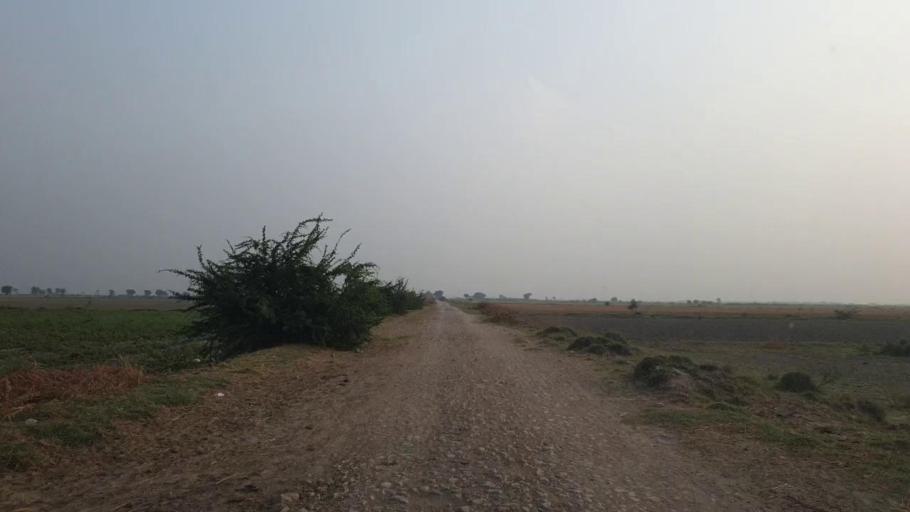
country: PK
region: Sindh
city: Mirpur Batoro
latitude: 24.6587
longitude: 68.3726
